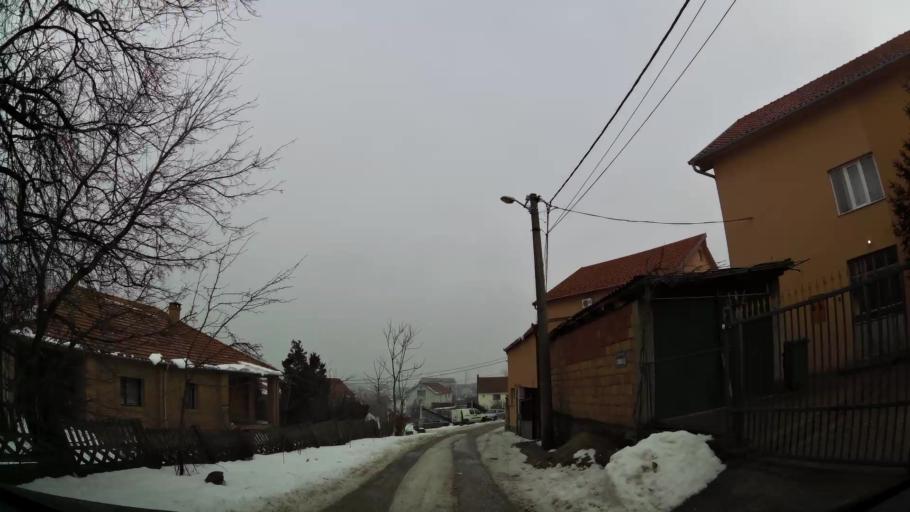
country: RS
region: Central Serbia
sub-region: Belgrade
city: Zvezdara
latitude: 44.7558
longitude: 20.5326
